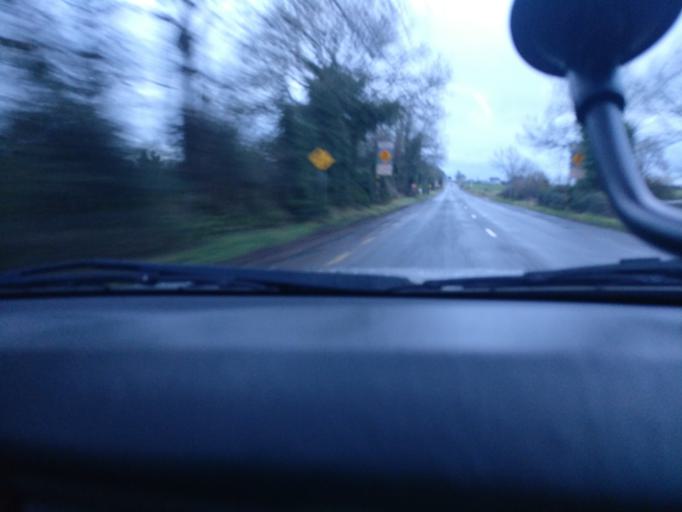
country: IE
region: Connaught
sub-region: County Galway
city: Loughrea
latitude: 53.2373
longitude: -8.4525
